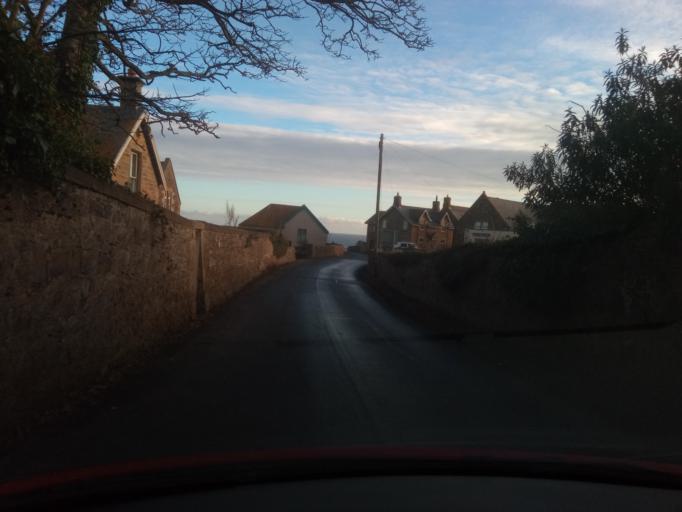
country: GB
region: Scotland
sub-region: The Scottish Borders
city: Eyemouth
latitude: 55.8998
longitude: -2.1333
